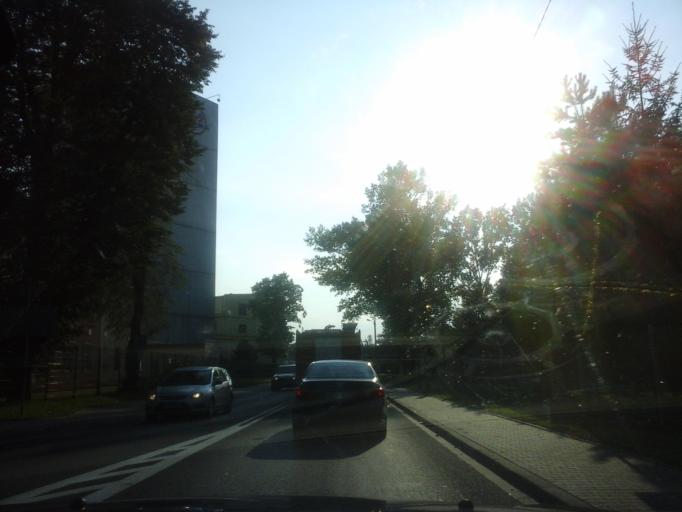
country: PL
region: Lesser Poland Voivodeship
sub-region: Powiat krakowski
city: Skawina
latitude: 49.9739
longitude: 19.8144
